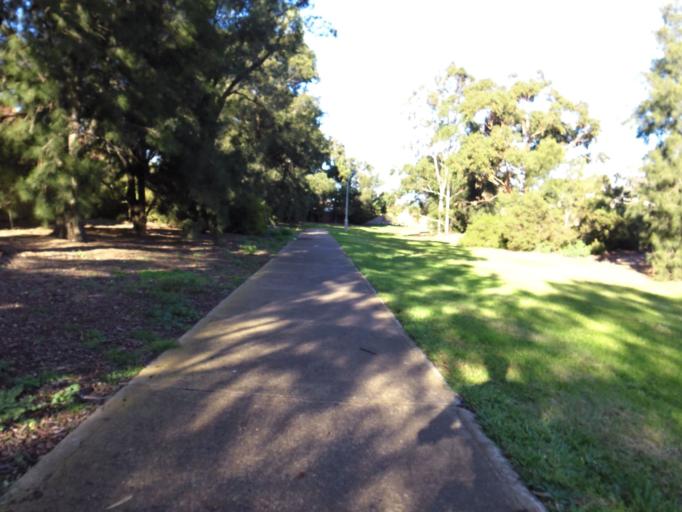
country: AU
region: Victoria
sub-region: Wyndham
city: Hoppers Crossing
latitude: -37.8656
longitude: 144.6936
